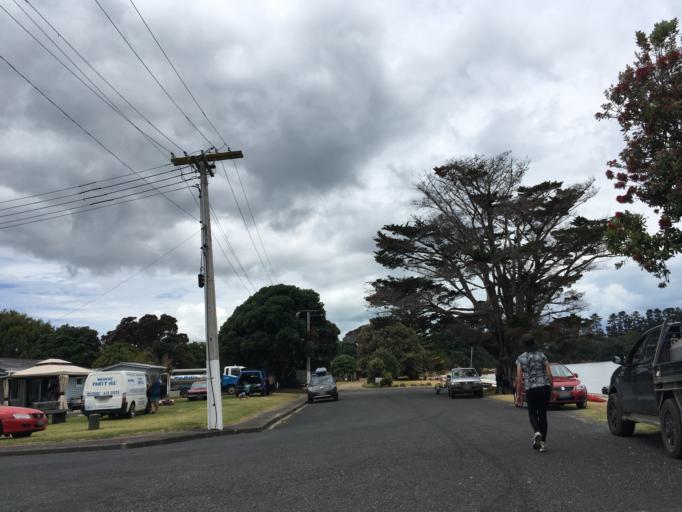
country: NZ
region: Auckland
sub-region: Auckland
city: Pakuranga
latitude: -36.7936
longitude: 175.0233
